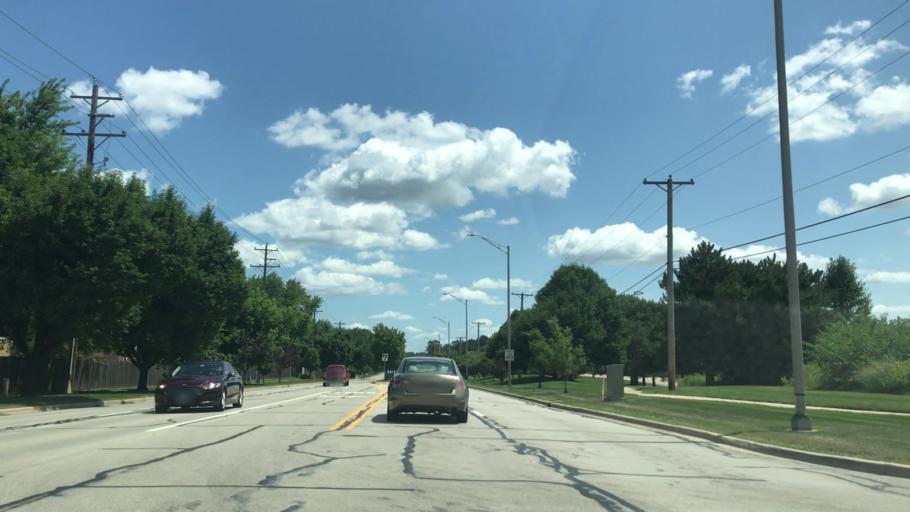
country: US
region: Illinois
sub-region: DuPage County
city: Naperville
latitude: 41.7655
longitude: -88.1817
